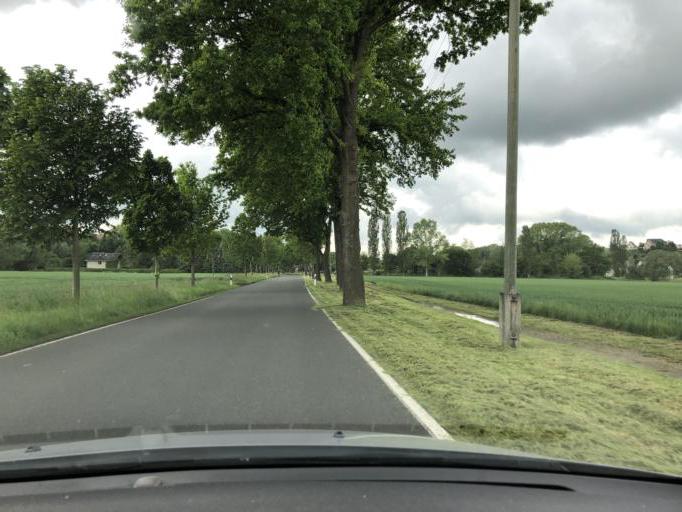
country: DE
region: Saxony
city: Remse
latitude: 50.8572
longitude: 12.5813
